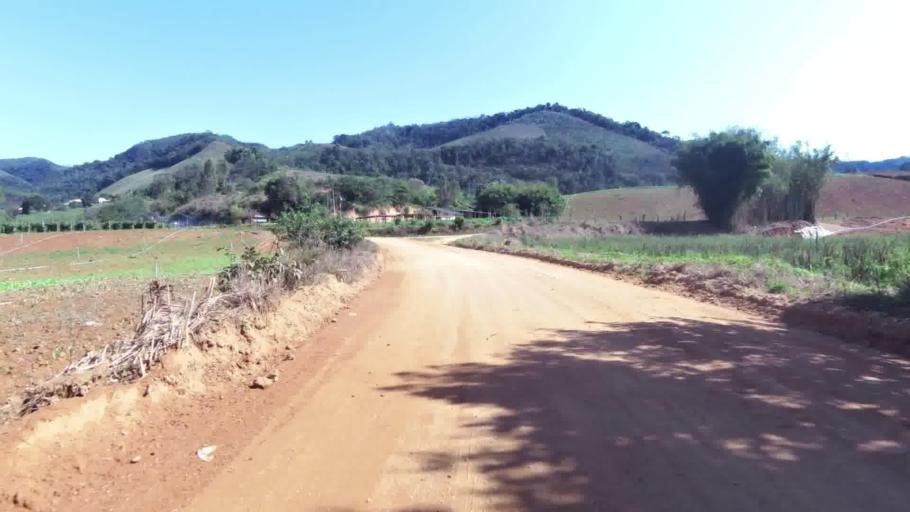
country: BR
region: Espirito Santo
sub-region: Alfredo Chaves
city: Alfredo Chaves
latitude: -20.5317
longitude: -40.8401
